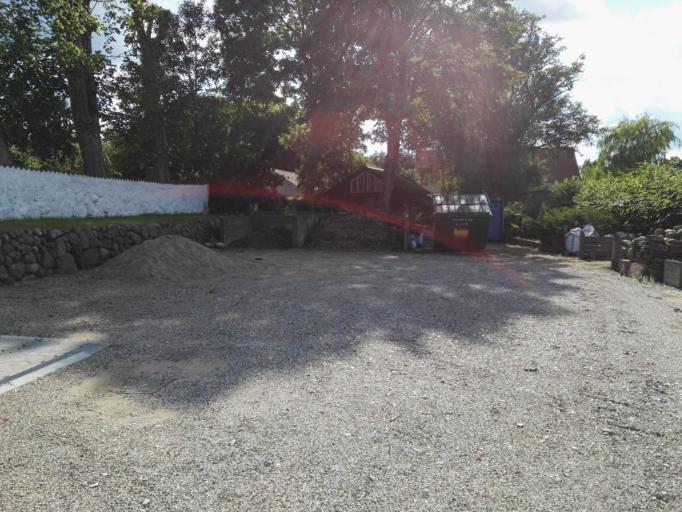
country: DK
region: Capital Region
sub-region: Frederikssund Kommune
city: Frederikssund
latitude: 55.8212
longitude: 12.1006
